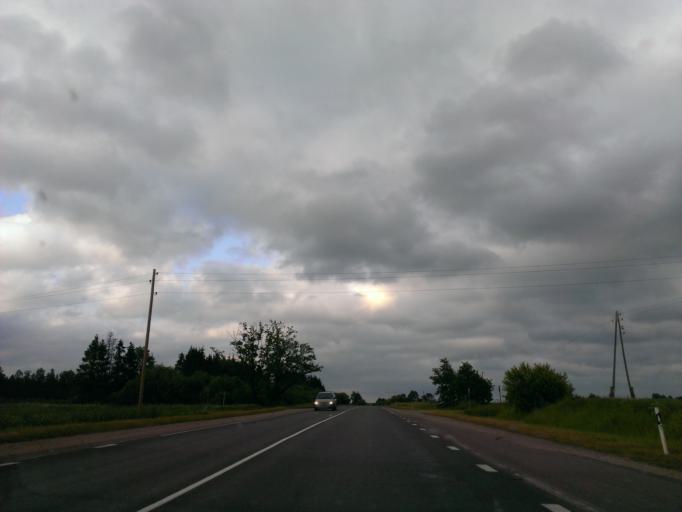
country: LV
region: Skrunda
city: Skrunda
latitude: 56.6771
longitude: 22.1648
